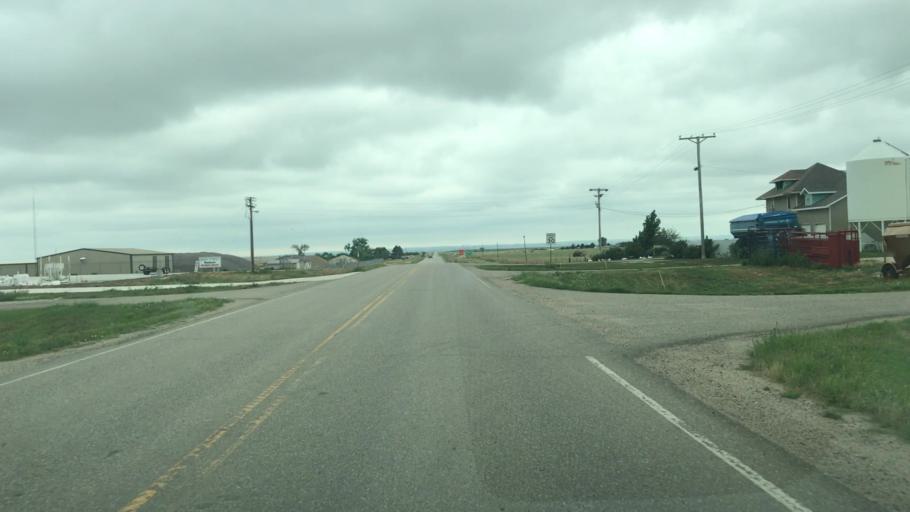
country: US
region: South Dakota
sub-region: Jackson County
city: Kadoka
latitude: 43.8349
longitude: -101.5225
